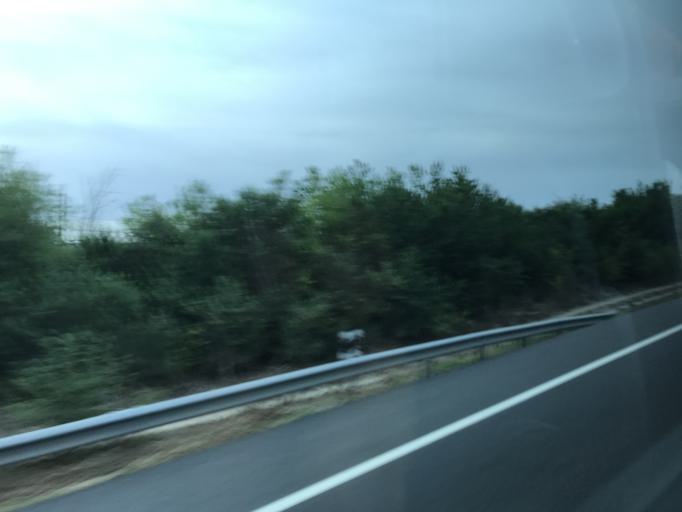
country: ES
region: Castille and Leon
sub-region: Provincia de Segovia
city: Tolocirio
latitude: 41.1296
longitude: -4.6465
